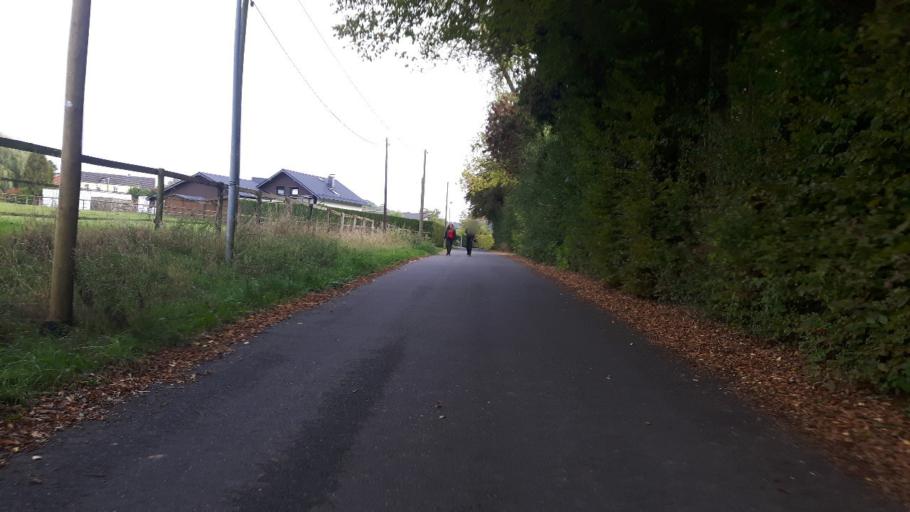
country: DE
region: North Rhine-Westphalia
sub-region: Regierungsbezirk Koln
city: Eitorf
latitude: 50.7681
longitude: 7.3912
